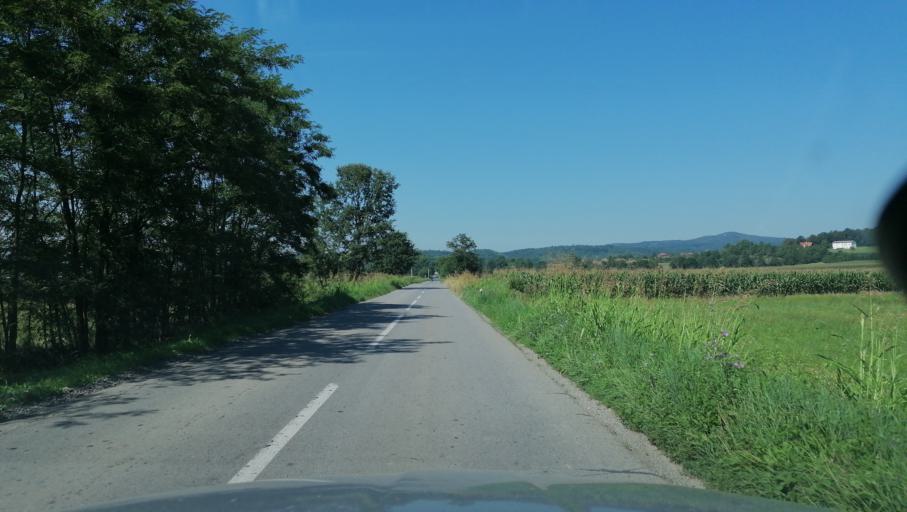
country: RS
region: Central Serbia
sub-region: Raski Okrug
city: Vrnjacka Banja
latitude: 43.7163
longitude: 20.8216
